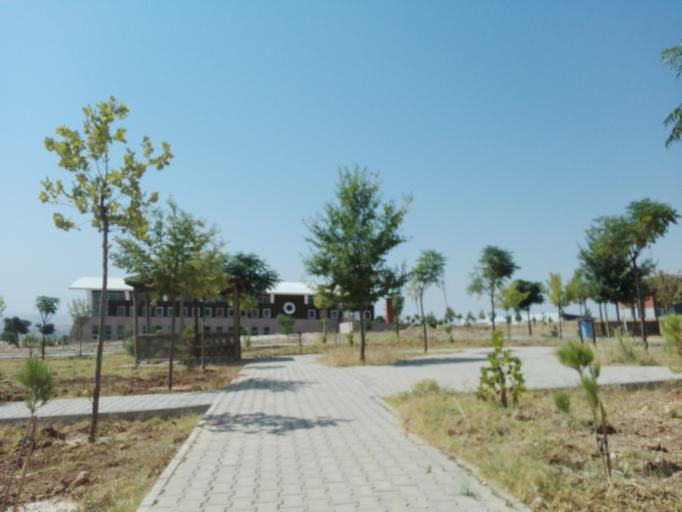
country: TR
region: Batman
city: Oymatas
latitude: 37.7913
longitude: 41.0653
